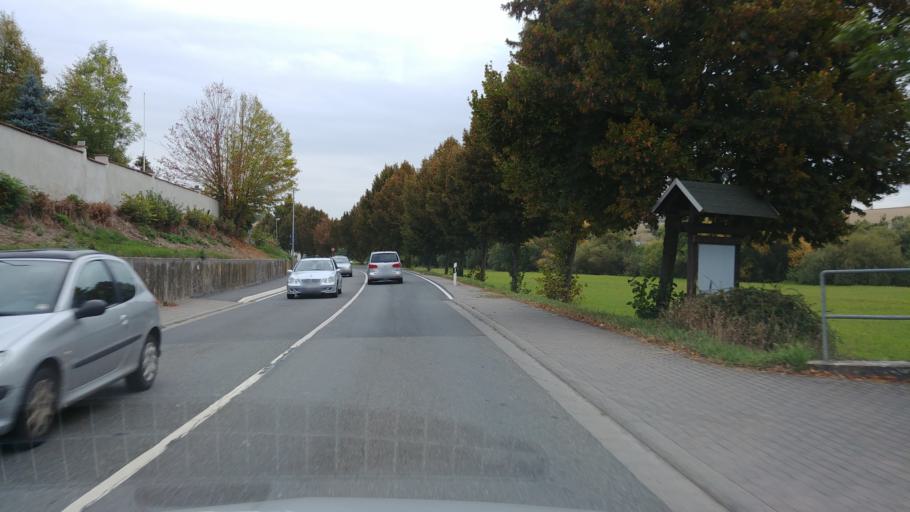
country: DE
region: Rheinland-Pfalz
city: Holzheim
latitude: 50.3479
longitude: 8.0479
